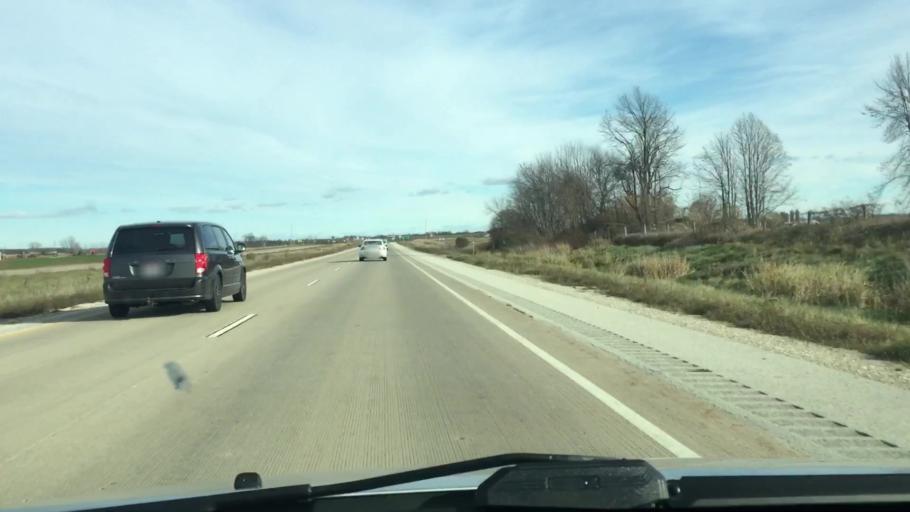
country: US
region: Wisconsin
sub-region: Kewaunee County
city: Luxemburg
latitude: 44.7161
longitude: -87.6568
